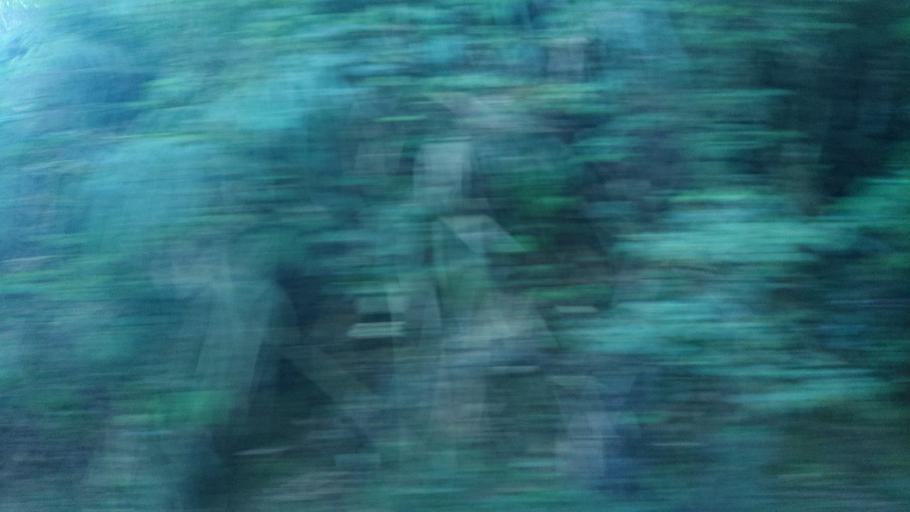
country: TW
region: Taiwan
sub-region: Chiayi
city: Jiayi Shi
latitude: 23.5350
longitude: 120.6366
